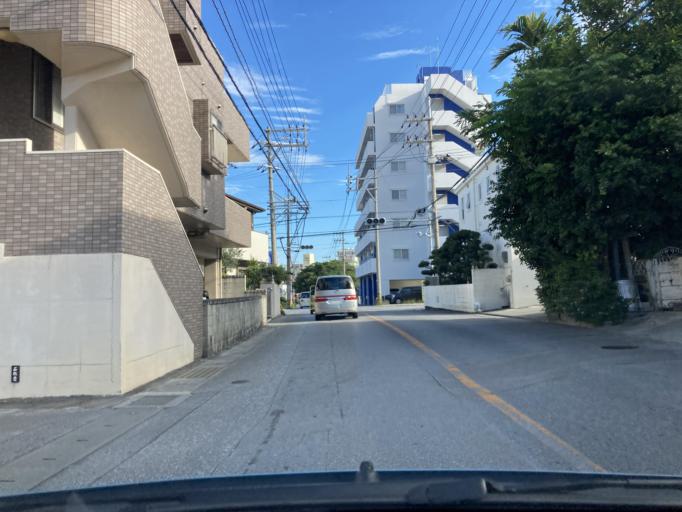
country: JP
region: Okinawa
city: Ginowan
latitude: 26.2729
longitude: 127.7410
